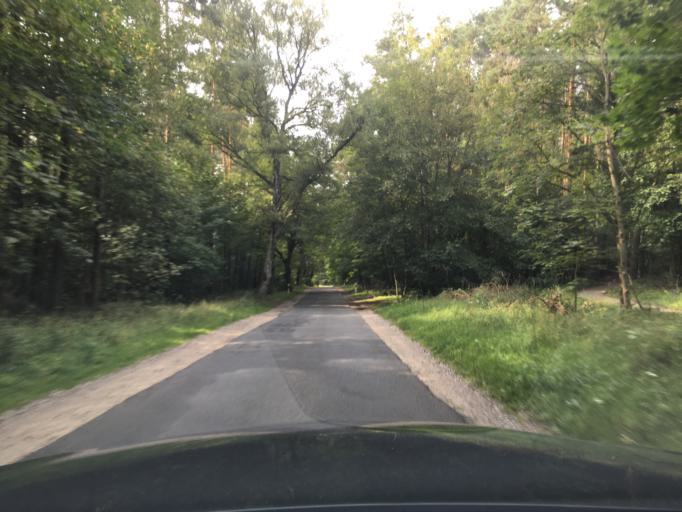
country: DE
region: Mecklenburg-Vorpommern
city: Waren
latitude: 53.4760
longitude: 12.7771
